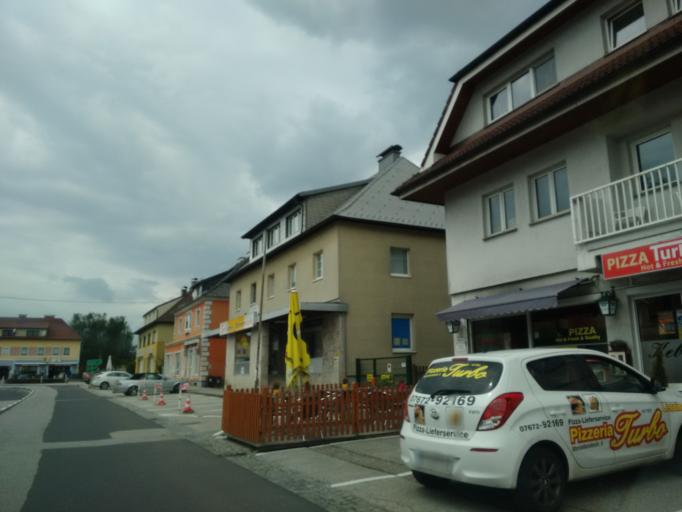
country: AT
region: Upper Austria
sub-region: Politischer Bezirk Vocklabruck
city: Lenzing
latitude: 47.9798
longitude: 13.6133
